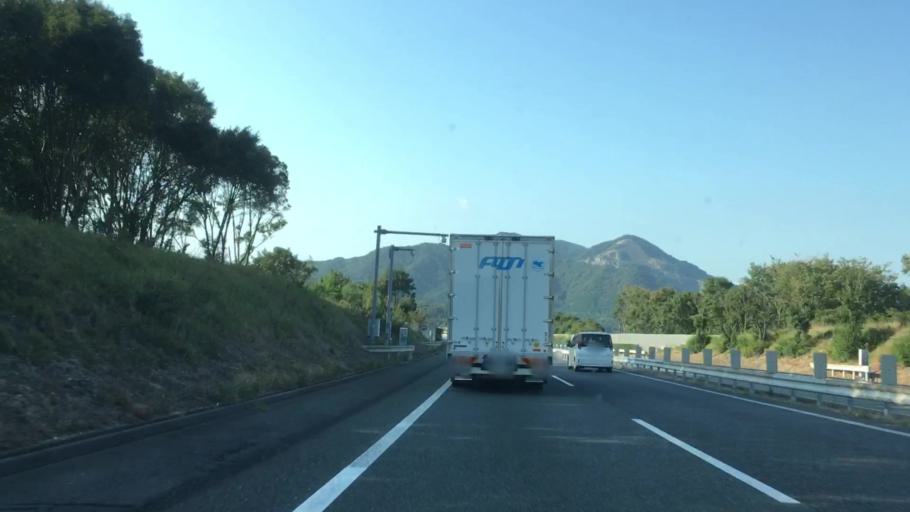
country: JP
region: Yamaguchi
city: Hofu
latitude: 34.0668
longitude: 131.5003
